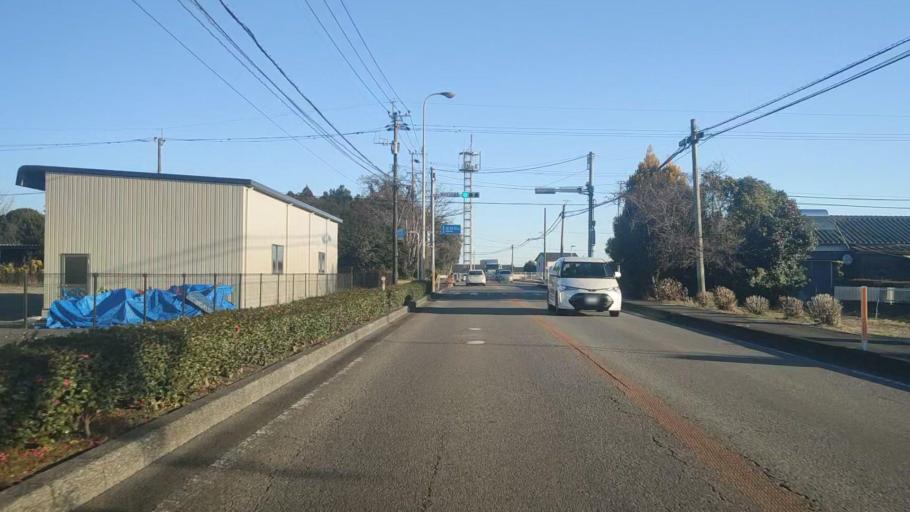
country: JP
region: Miyazaki
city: Takanabe
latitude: 32.1770
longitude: 131.5211
